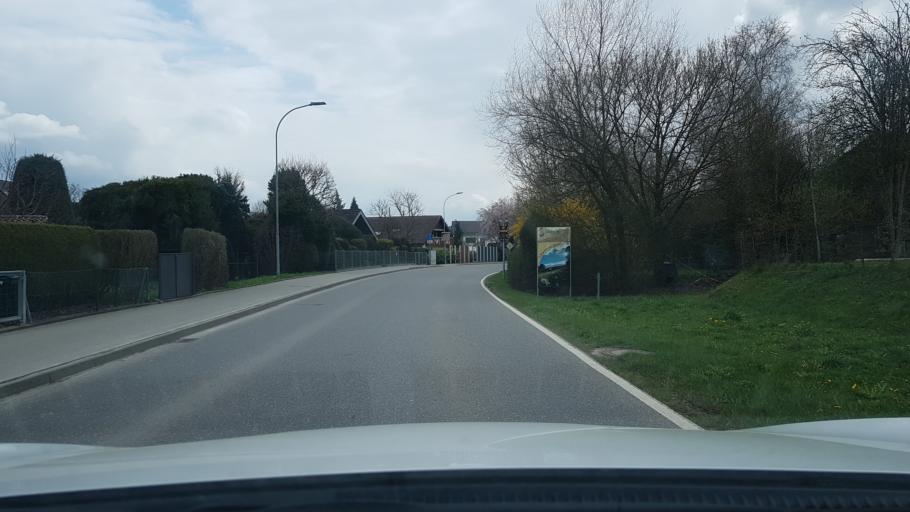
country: DE
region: Baden-Wuerttemberg
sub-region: Tuebingen Region
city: Warthausen
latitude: 48.1776
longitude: 9.7909
